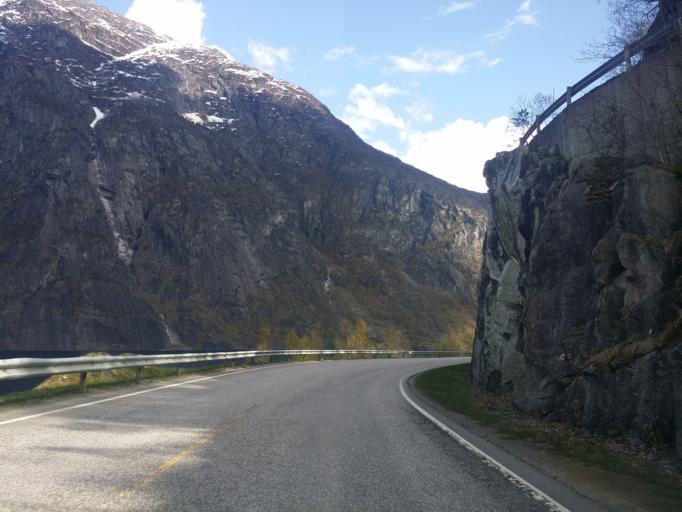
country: NO
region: Hordaland
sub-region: Eidfjord
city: Eidfjord
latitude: 60.4463
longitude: 7.1021
